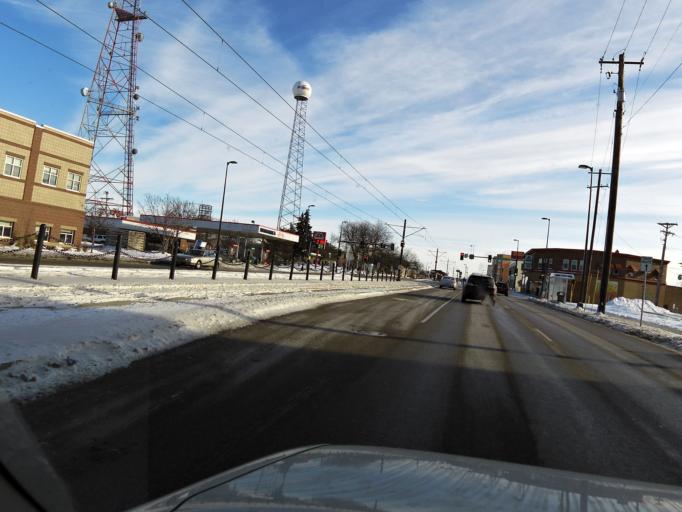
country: US
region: Minnesota
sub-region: Ramsey County
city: Lauderdale
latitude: 44.9687
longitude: -93.2097
